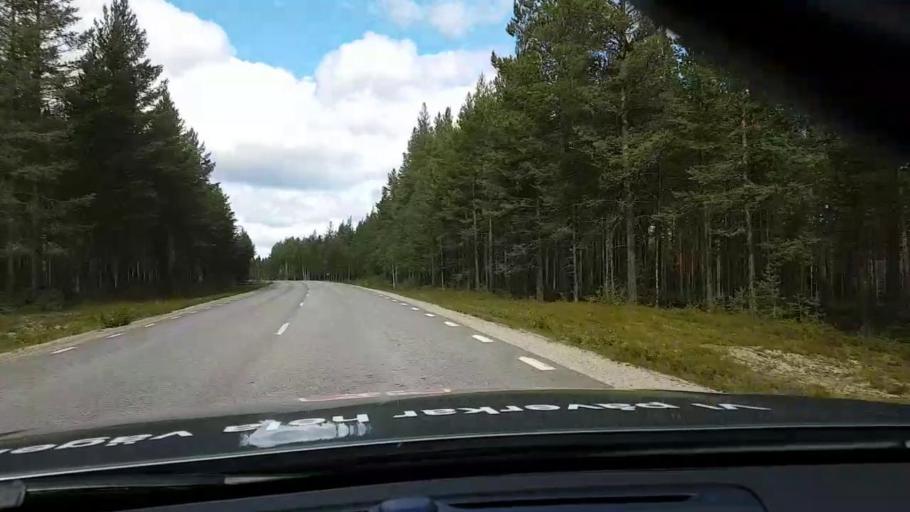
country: SE
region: Vaesternorrland
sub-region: OErnskoeldsviks Kommun
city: Bredbyn
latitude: 63.5353
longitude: 17.9658
